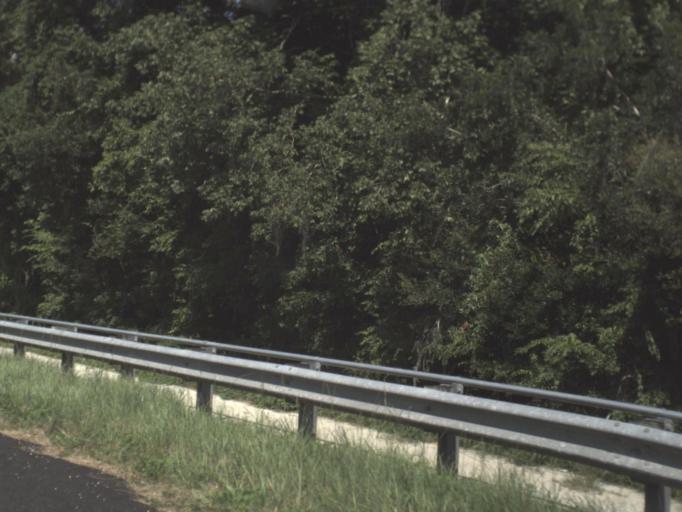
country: US
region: Florida
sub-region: Hernando County
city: North Brooksville
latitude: 28.5502
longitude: -82.4254
